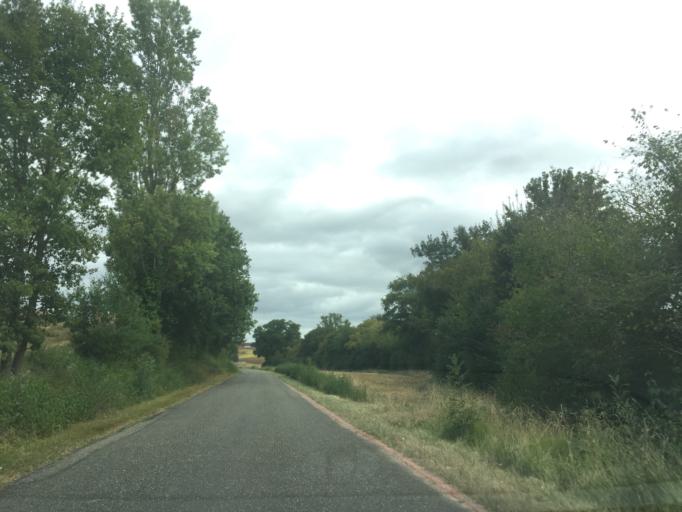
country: FR
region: Midi-Pyrenees
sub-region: Departement du Gers
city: Vic-Fezensac
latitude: 43.6667
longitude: 0.3555
